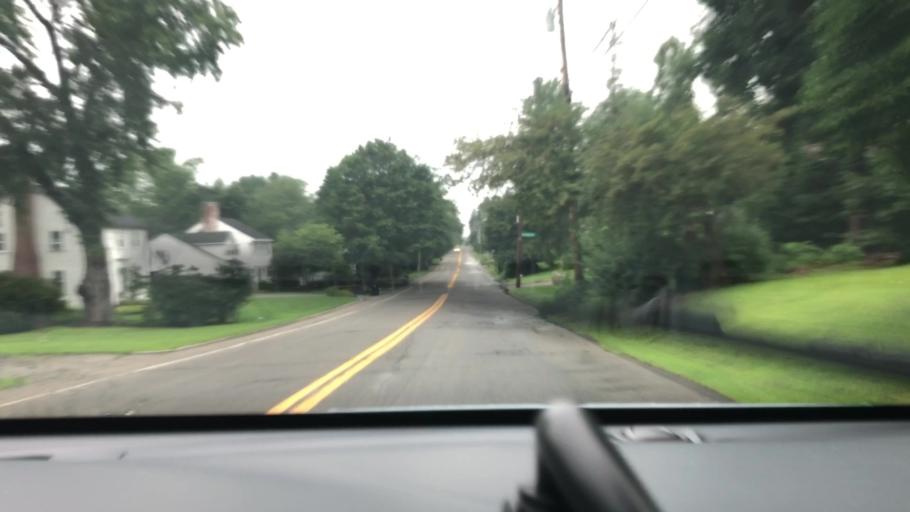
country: US
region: New Hampshire
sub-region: Merrimack County
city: South Hooksett
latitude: 43.0243
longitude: -71.4624
